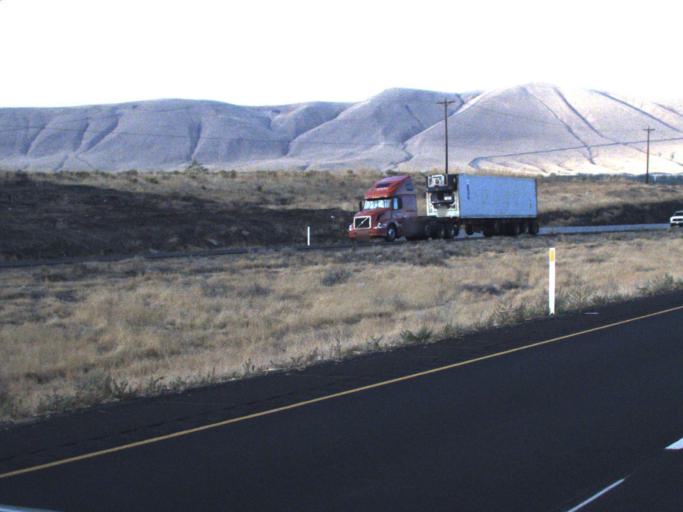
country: US
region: Washington
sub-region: Benton County
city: Benton City
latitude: 46.2555
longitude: -119.4577
